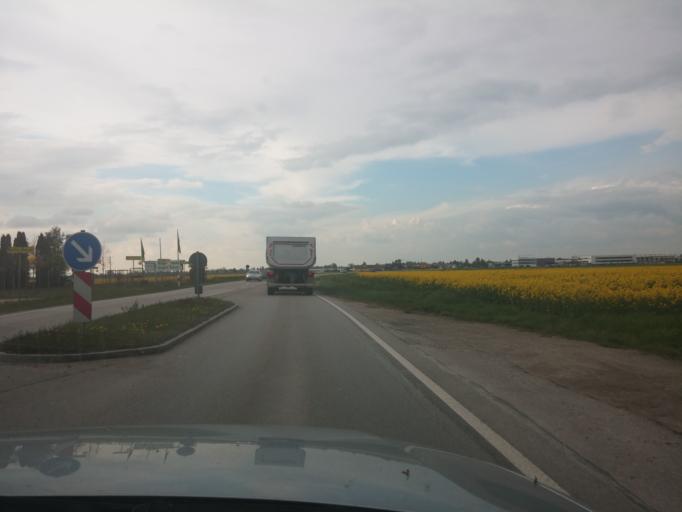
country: DE
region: Bavaria
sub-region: Upper Bavaria
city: Feldkirchen
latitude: 48.1328
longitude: 11.7377
